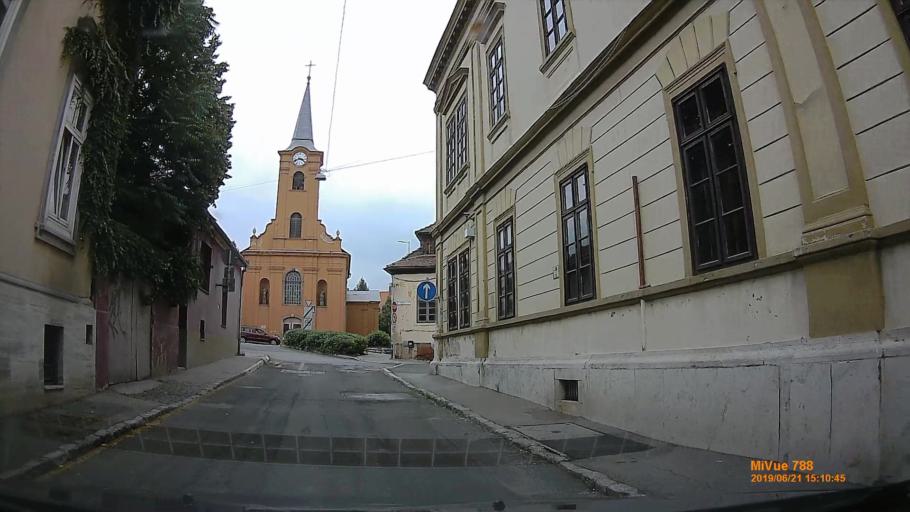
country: HU
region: Baranya
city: Pecs
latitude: 46.0790
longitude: 18.2346
